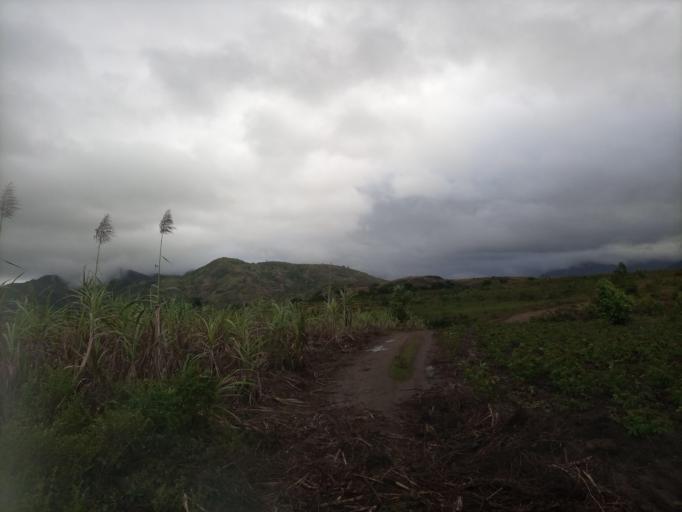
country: MG
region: Anosy
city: Fort Dauphin
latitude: -24.7603
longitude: 47.0682
